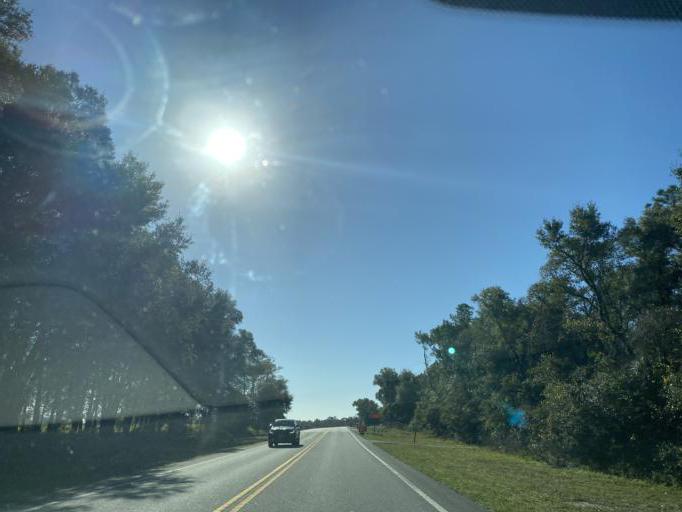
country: US
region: Florida
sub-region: Lake County
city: Mount Plymouth
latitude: 28.8384
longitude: -81.5271
